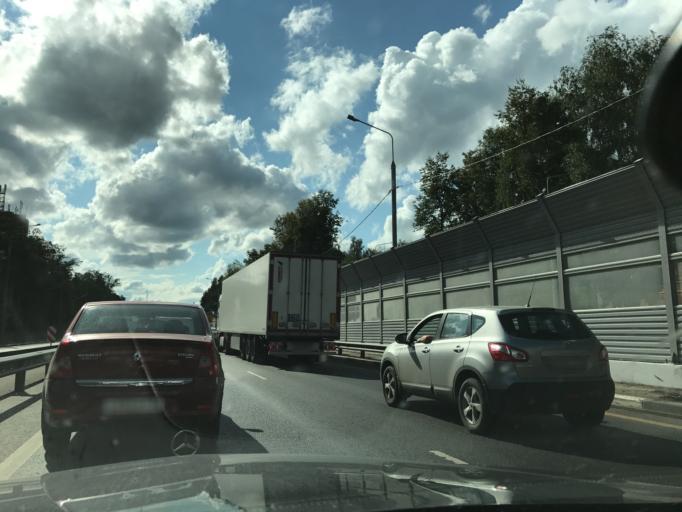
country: RU
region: Vladimir
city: Lakinsk
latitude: 56.0132
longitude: 39.9485
